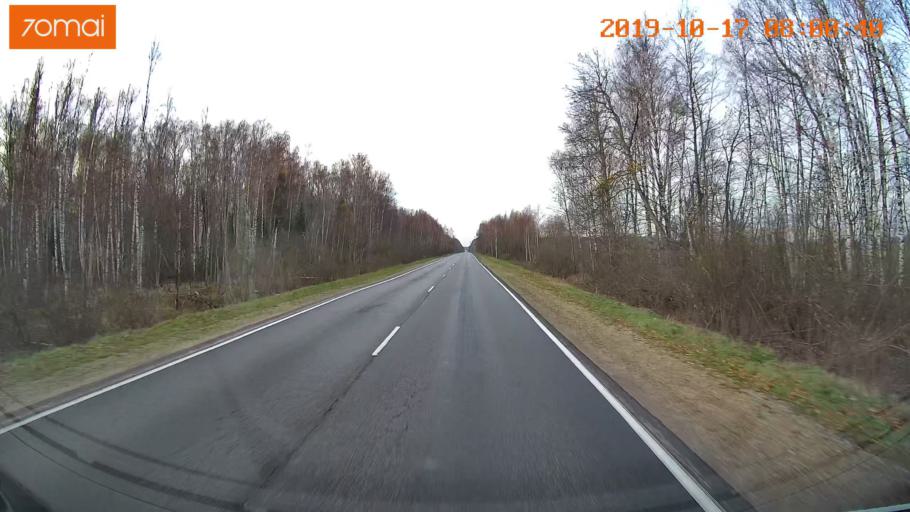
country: RU
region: Vladimir
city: Bavleny
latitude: 56.3810
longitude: 39.5132
